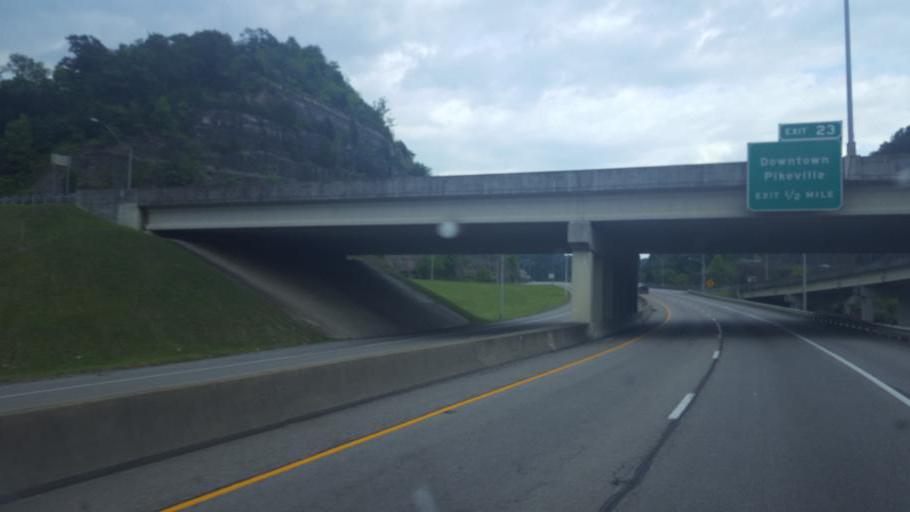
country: US
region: Kentucky
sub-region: Pike County
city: Pikeville
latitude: 37.4798
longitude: -82.5431
